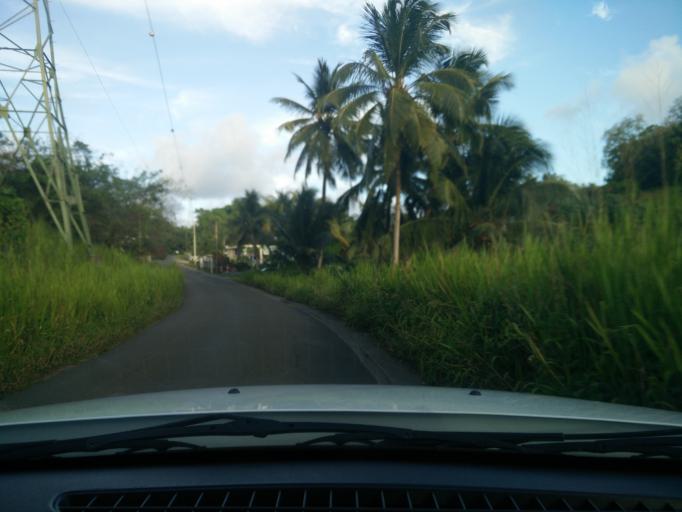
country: GP
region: Guadeloupe
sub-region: Guadeloupe
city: Les Abymes
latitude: 16.2505
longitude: -61.4986
